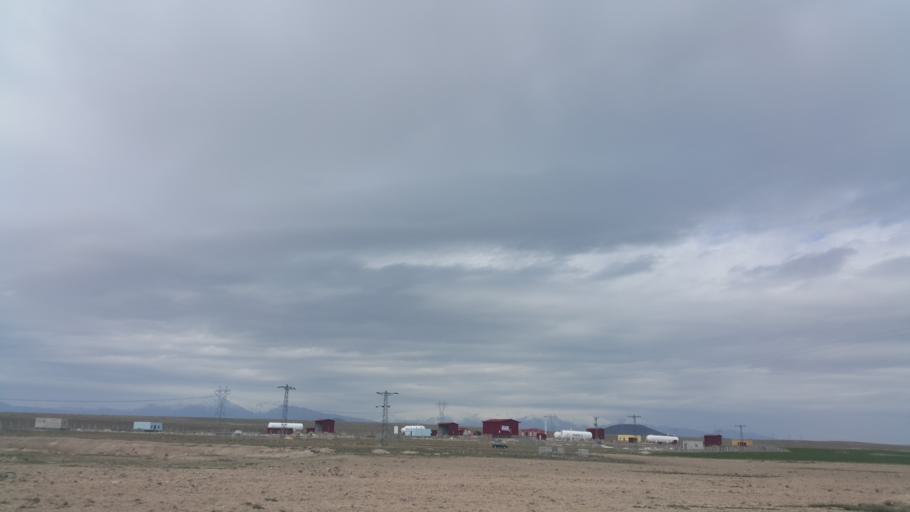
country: TR
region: Nigde
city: Altunhisar
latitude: 37.8947
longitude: 34.1366
